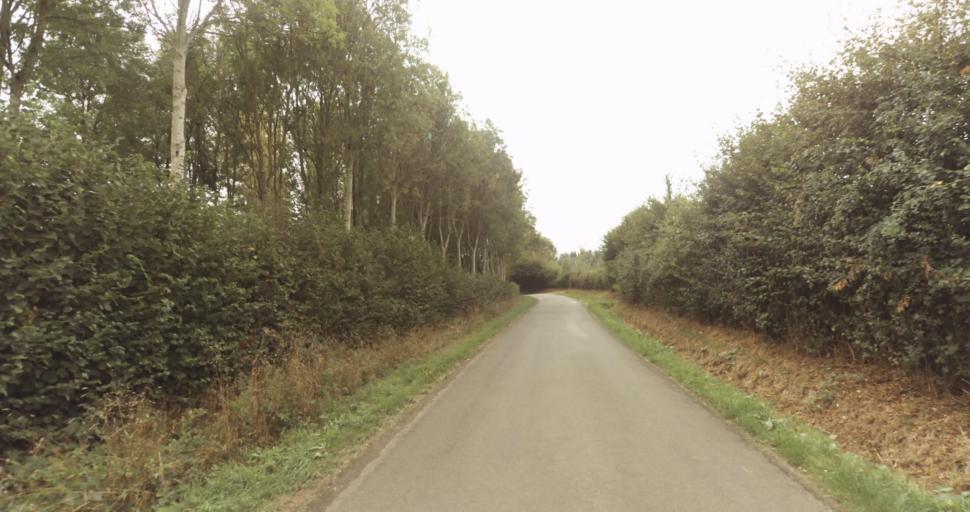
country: FR
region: Lower Normandy
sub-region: Departement de l'Orne
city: Gace
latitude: 48.8174
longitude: 0.3641
